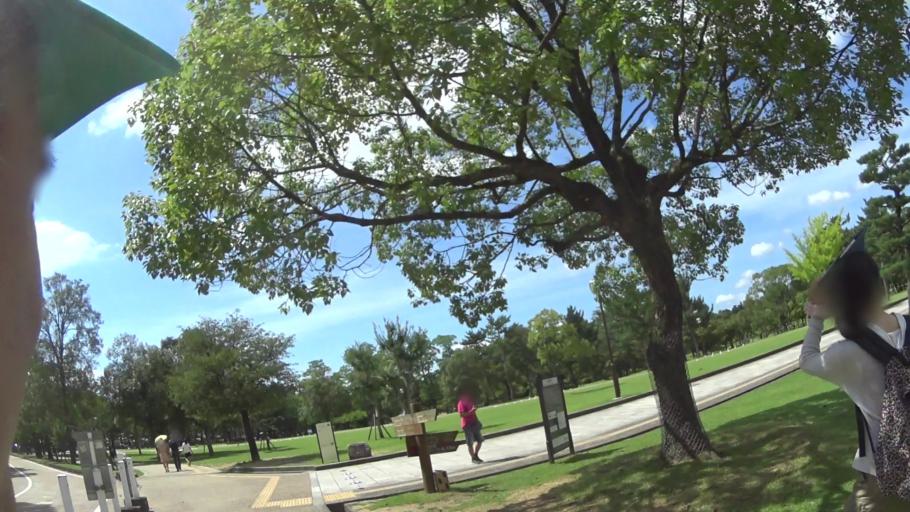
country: JP
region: Nara
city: Nara-shi
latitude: 34.6833
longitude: 135.8424
